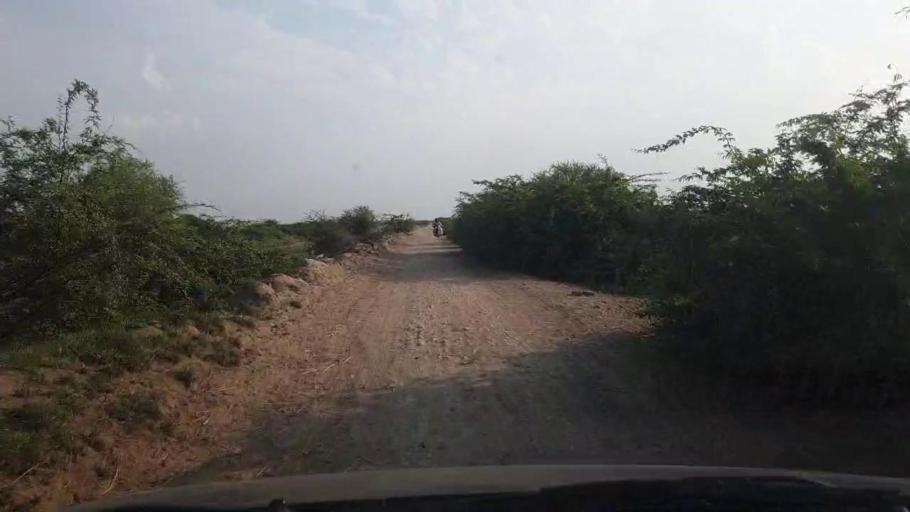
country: PK
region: Sindh
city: Badin
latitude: 24.5641
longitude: 68.6678
